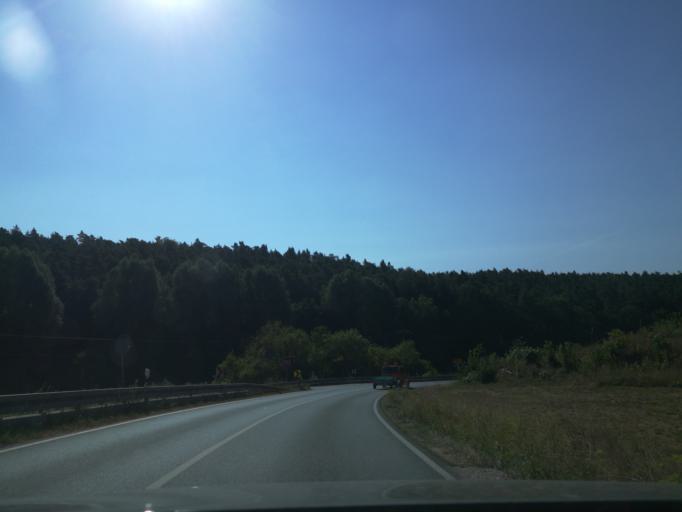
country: DE
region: Bavaria
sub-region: Regierungsbezirk Mittelfranken
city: Ammerndorf
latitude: 49.4359
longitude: 10.8548
